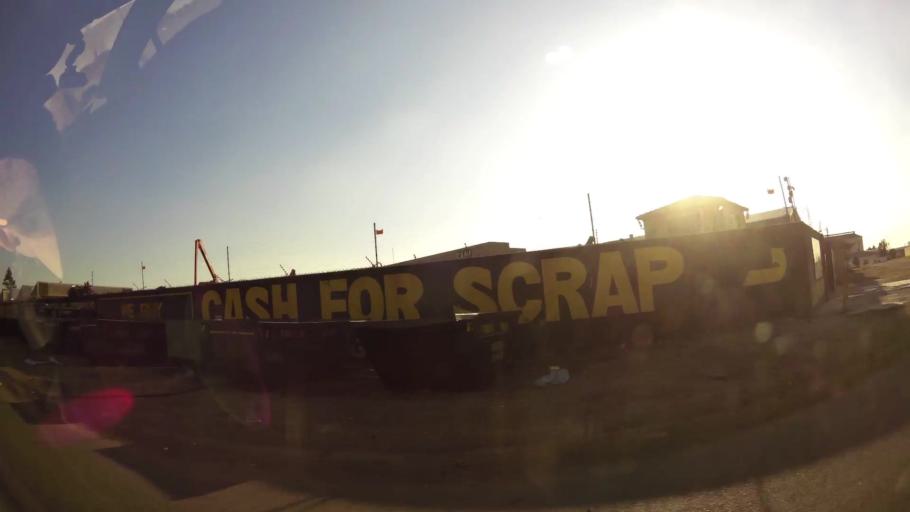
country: ZA
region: Gauteng
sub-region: West Rand District Municipality
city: Randfontein
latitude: -26.2017
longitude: 27.6958
